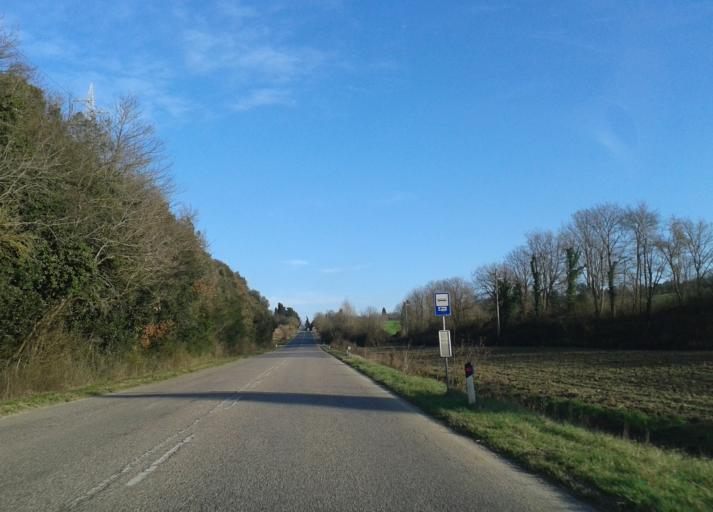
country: IT
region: Tuscany
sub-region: Provincia di Livorno
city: Guasticce
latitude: 43.5701
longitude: 10.4075
